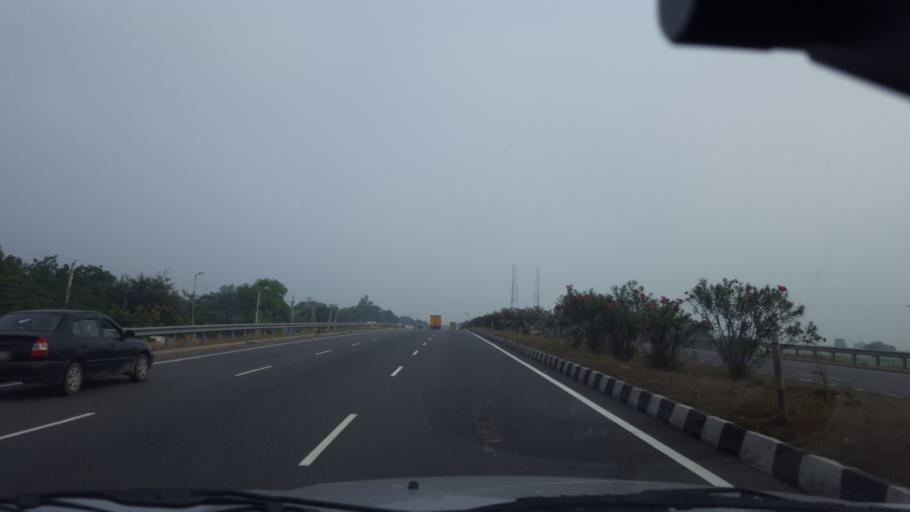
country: IN
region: Andhra Pradesh
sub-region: Guntur
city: Chilakalurupet
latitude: 16.0439
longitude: 80.1381
